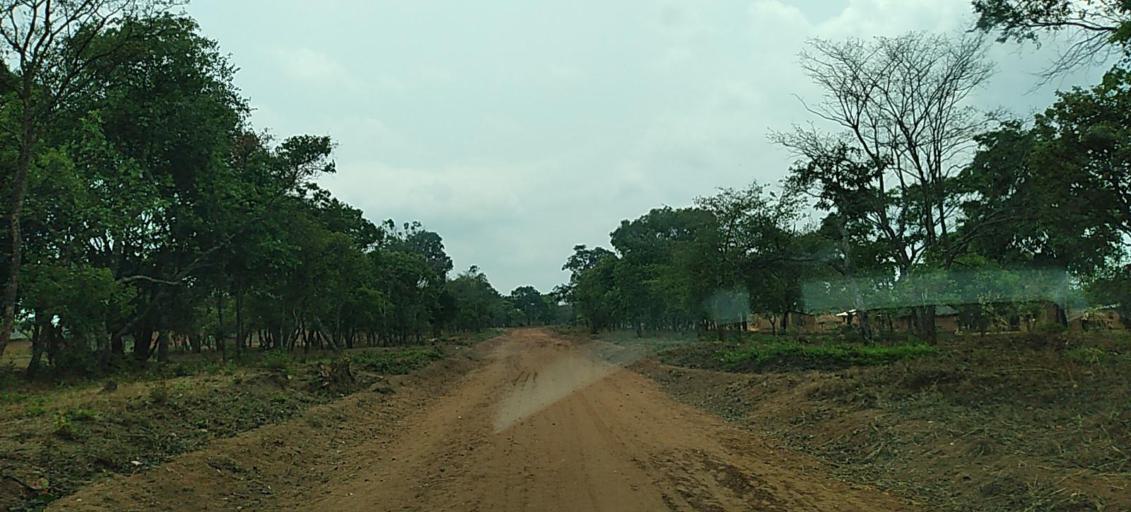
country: ZM
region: North-Western
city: Mwinilunga
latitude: -11.4485
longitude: 24.7505
